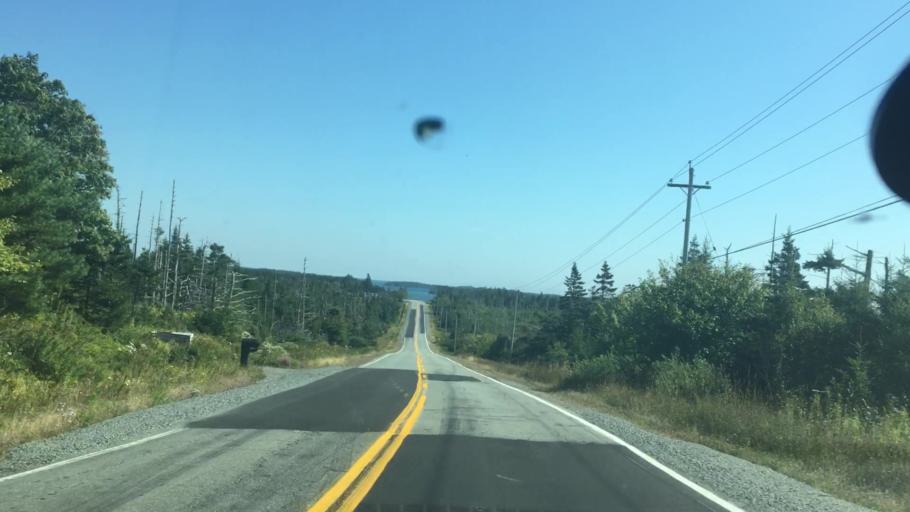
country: CA
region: Nova Scotia
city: New Glasgow
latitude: 44.9157
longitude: -62.3157
